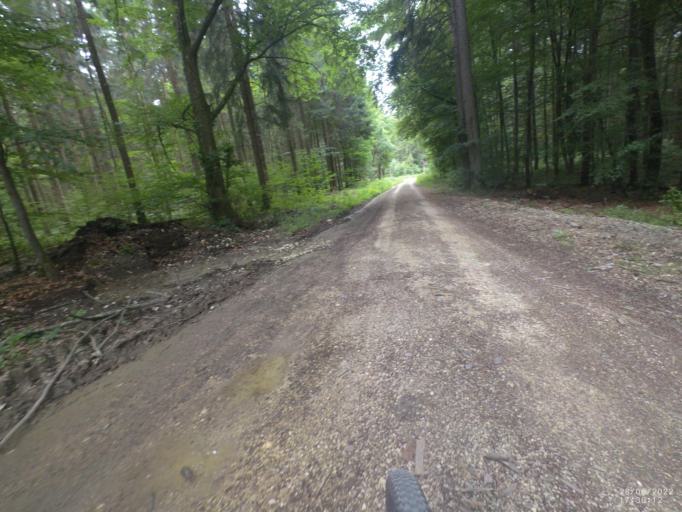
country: DE
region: Baden-Wuerttemberg
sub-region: Regierungsbezirk Stuttgart
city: Gerstetten
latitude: 48.6510
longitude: 10.0286
